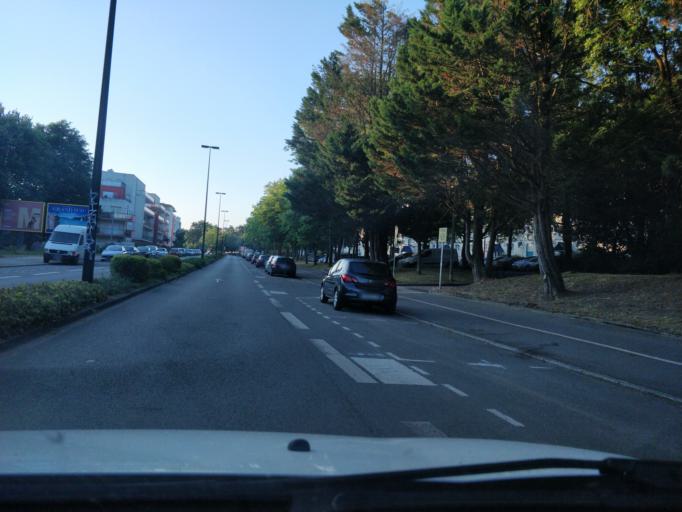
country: FR
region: Pays de la Loire
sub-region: Departement de la Loire-Atlantique
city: La Chapelle-sur-Erdre
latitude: 47.2621
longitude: -1.5662
